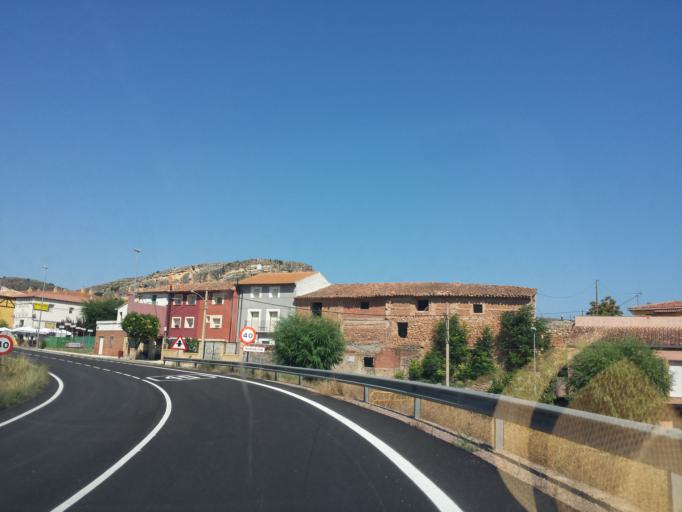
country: ES
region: Aragon
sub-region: Provincia de Zaragoza
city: Nuevalos
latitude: 41.2130
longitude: -1.7856
